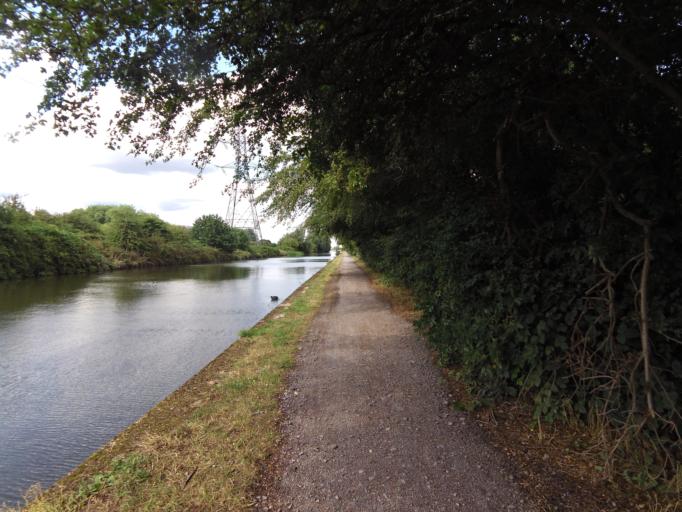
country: GB
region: England
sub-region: Greater London
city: Walthamstow
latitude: 51.6184
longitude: -0.0365
